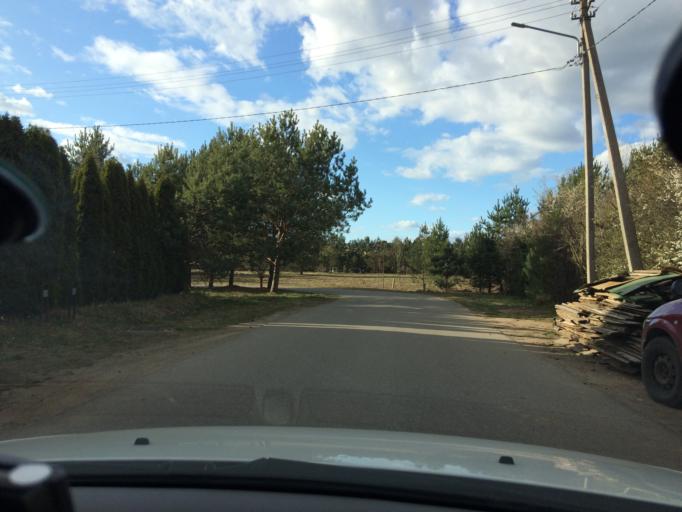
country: LT
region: Vilnius County
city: Rasos
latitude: 54.7769
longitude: 25.3475
